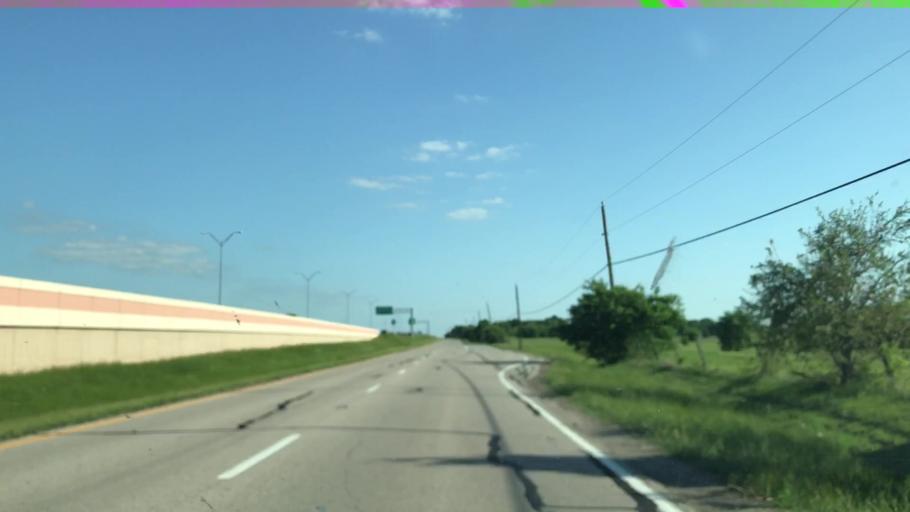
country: US
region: Texas
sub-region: Dallas County
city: Glenn Heights
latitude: 32.5548
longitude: -96.8228
